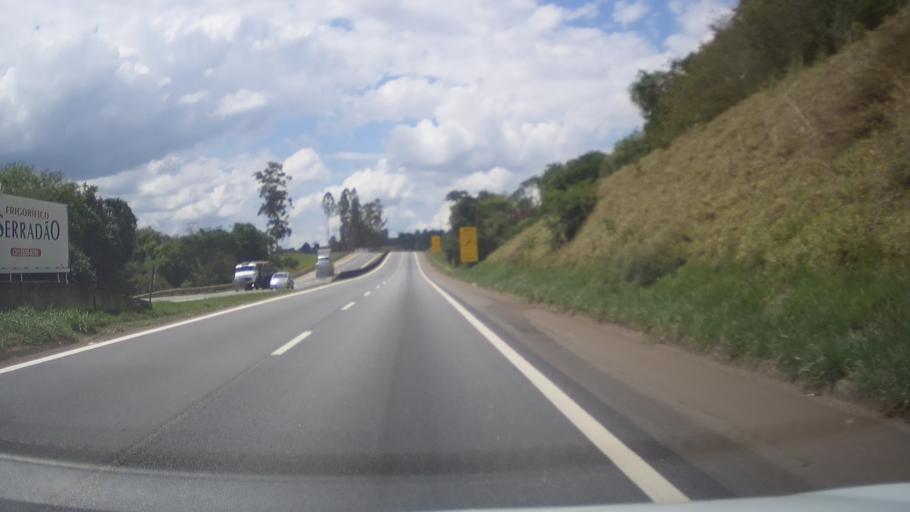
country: BR
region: Minas Gerais
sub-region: Nepomuceno
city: Nepomuceno
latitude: -21.2933
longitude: -45.1487
